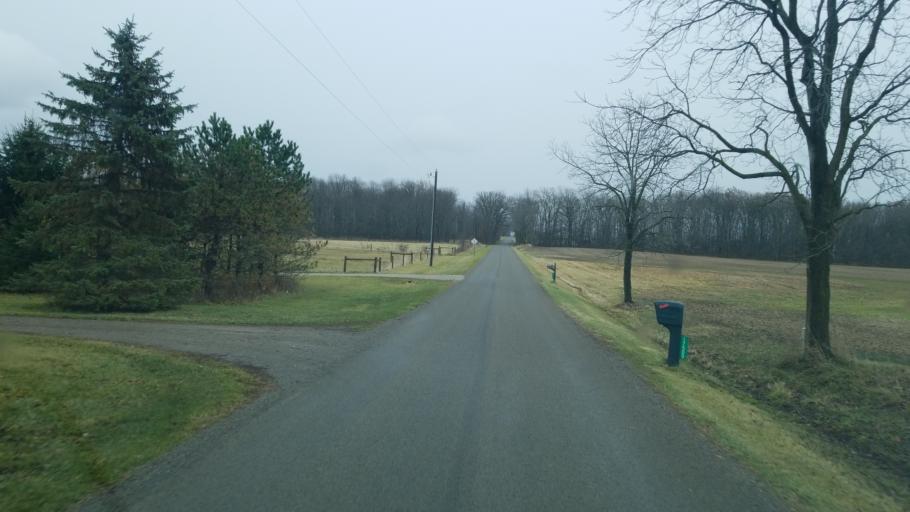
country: US
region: Ohio
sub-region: Union County
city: Marysville
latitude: 40.3342
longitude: -83.3868
